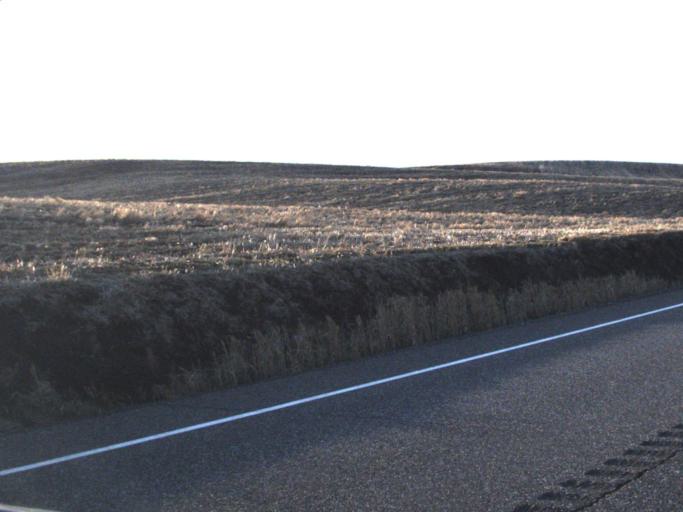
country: US
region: Washington
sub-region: Garfield County
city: Pomeroy
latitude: 46.7325
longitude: -117.7560
